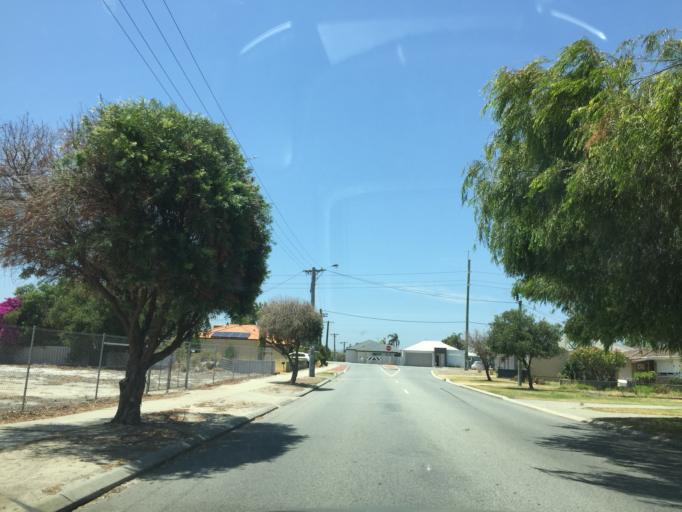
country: AU
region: Western Australia
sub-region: Canning
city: Cannington
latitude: -32.0133
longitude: 115.9482
